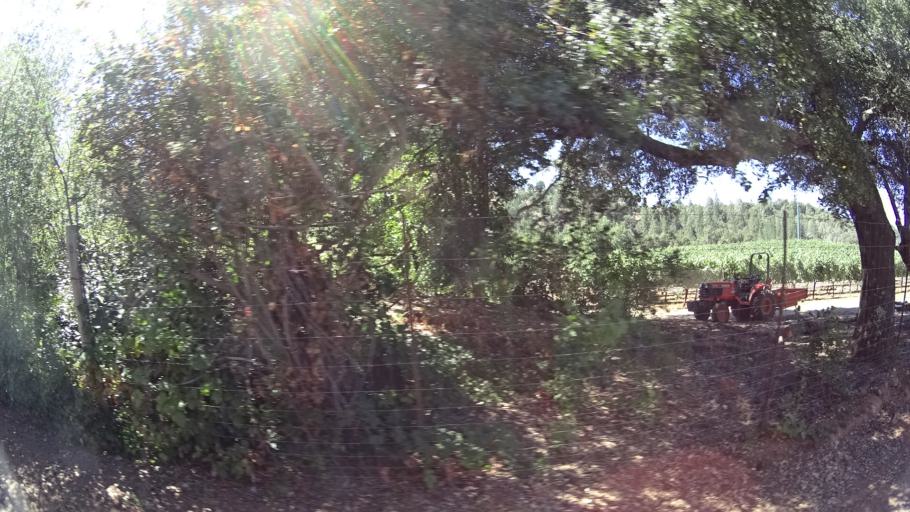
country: US
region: California
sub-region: Calaveras County
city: Mountain Ranch
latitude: 38.1511
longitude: -120.5490
